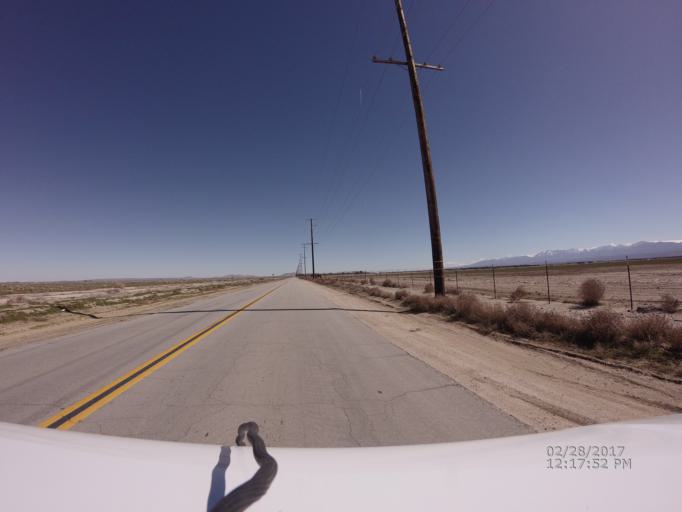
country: US
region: California
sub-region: Los Angeles County
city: Palmdale
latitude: 34.6314
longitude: -118.0571
